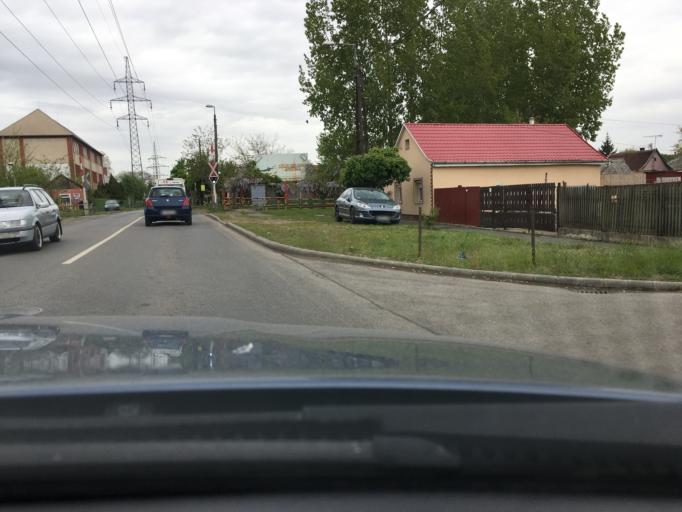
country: HU
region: Hajdu-Bihar
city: Debrecen
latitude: 47.5272
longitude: 21.6601
